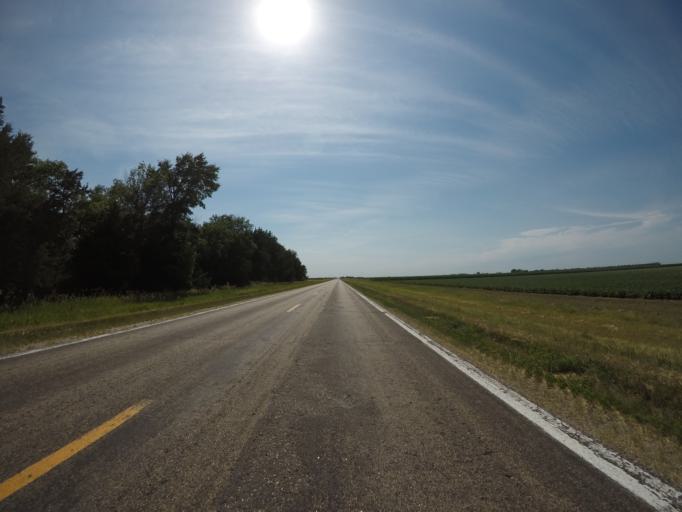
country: US
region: Nebraska
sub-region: Adams County
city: Hastings
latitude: 40.4375
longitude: -98.5041
